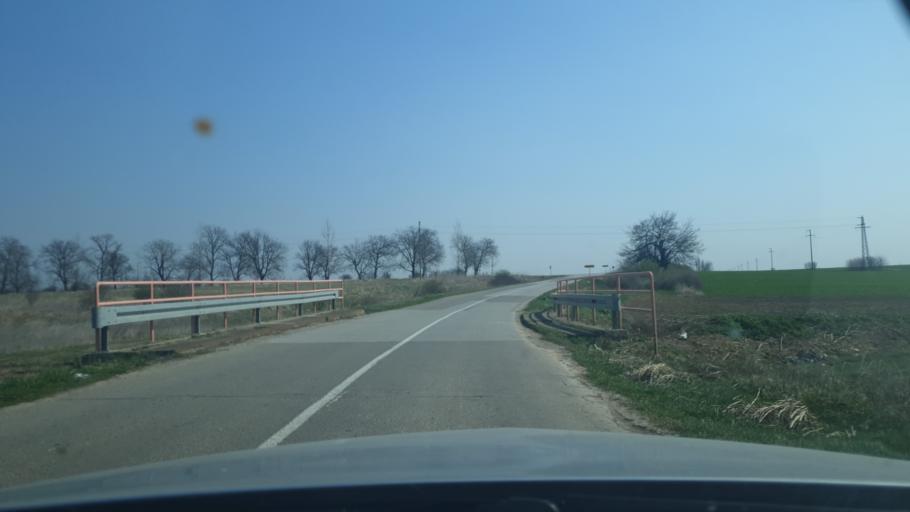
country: RS
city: Sasinci
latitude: 45.0475
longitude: 19.7193
